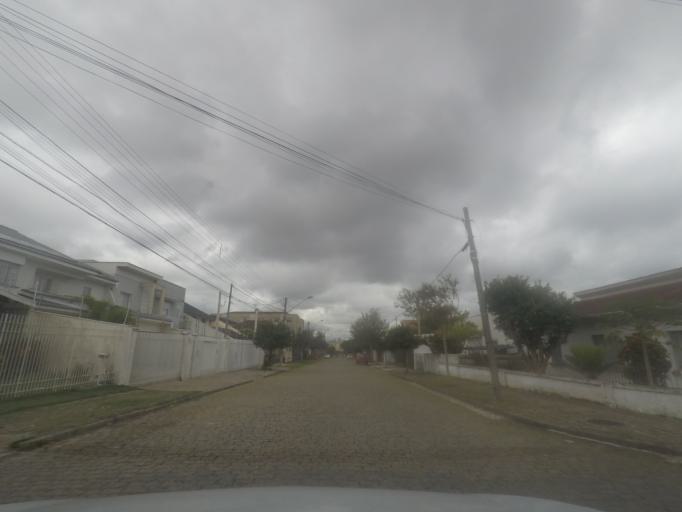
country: BR
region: Parana
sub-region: Curitiba
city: Curitiba
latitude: -25.4405
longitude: -49.2445
